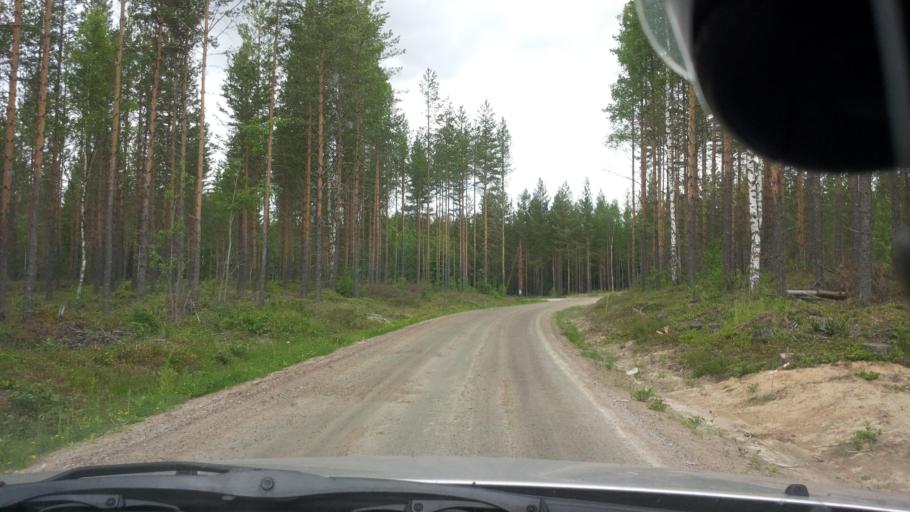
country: SE
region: Gaevleborg
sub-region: Ovanakers Kommun
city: Edsbyn
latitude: 61.5216
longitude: 15.3560
